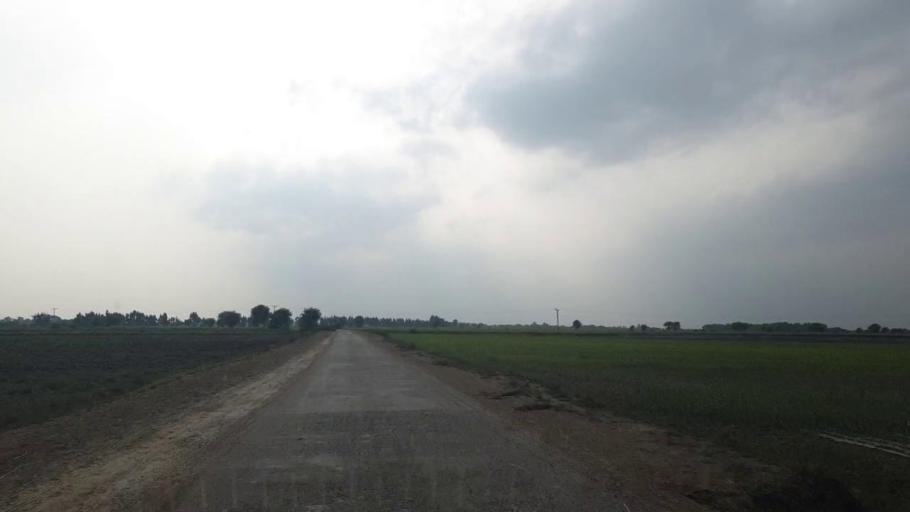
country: PK
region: Sindh
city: Badin
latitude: 24.6431
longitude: 68.6956
